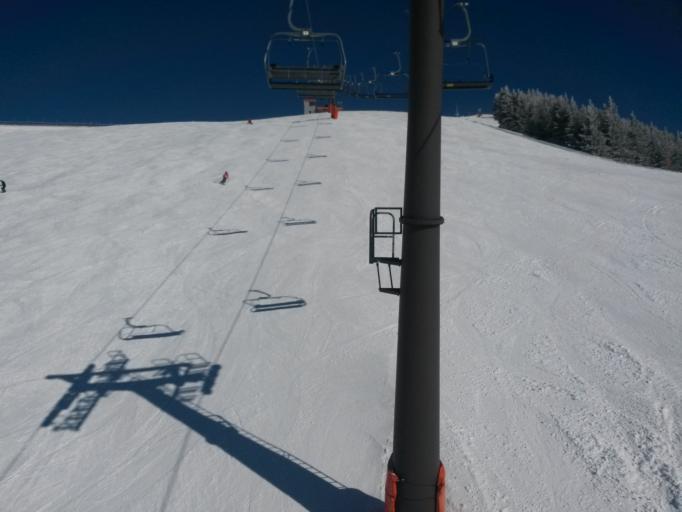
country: AT
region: Salzburg
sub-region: Politischer Bezirk Sankt Johann im Pongau
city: Dorfgastein
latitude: 47.2261
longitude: 13.1497
